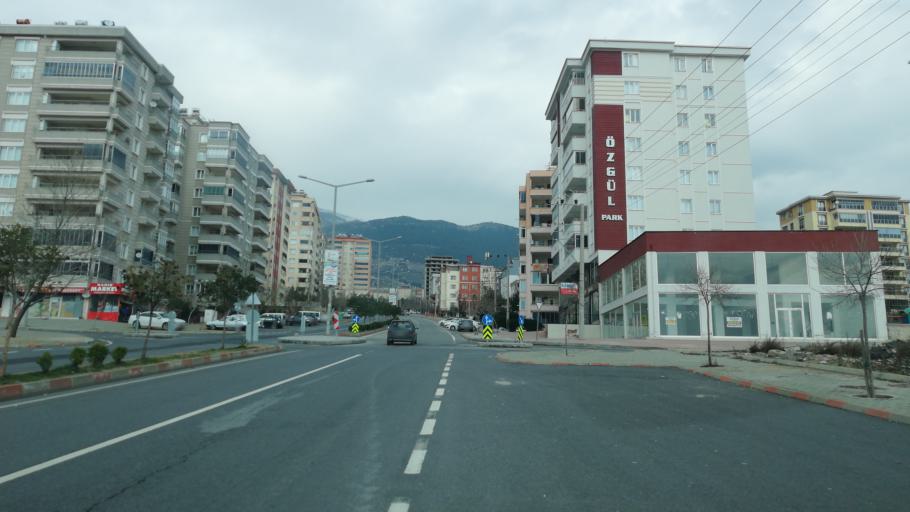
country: TR
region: Kahramanmaras
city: Kahramanmaras
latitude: 37.5886
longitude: 36.8627
